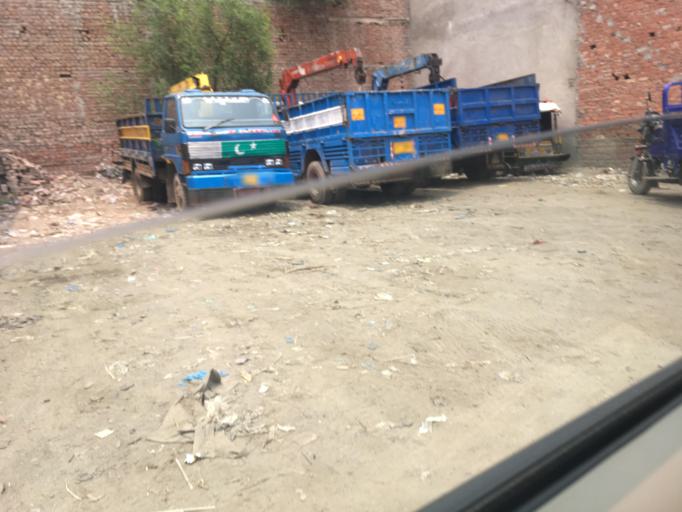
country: PK
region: Punjab
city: Lahore
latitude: 31.6128
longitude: 74.3507
